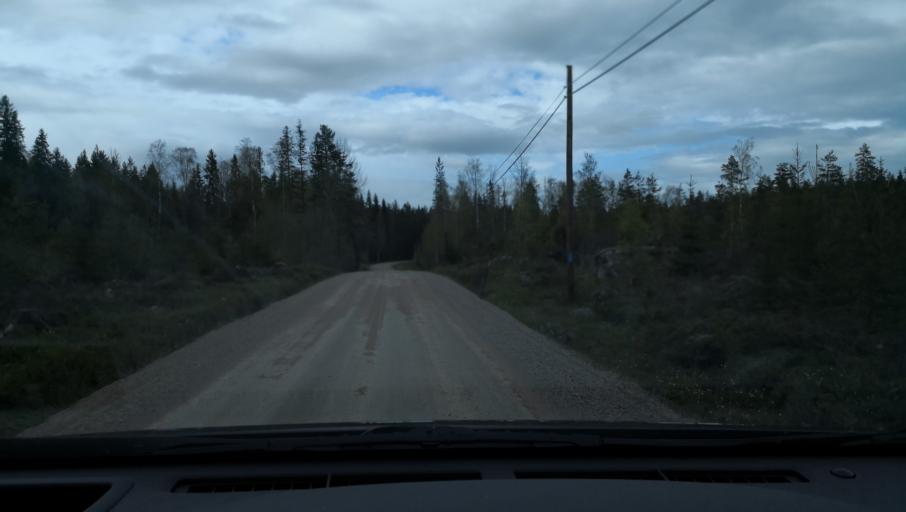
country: SE
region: Vaestmanland
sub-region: Fagersta Kommun
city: Fagersta
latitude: 60.1024
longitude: 15.7934
